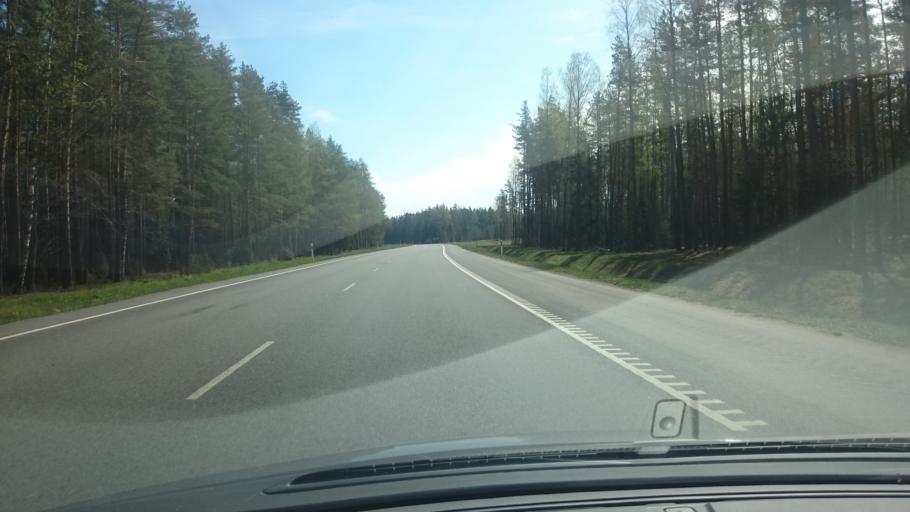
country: EE
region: Harju
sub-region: Loksa linn
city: Loksa
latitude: 59.4580
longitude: 25.8465
